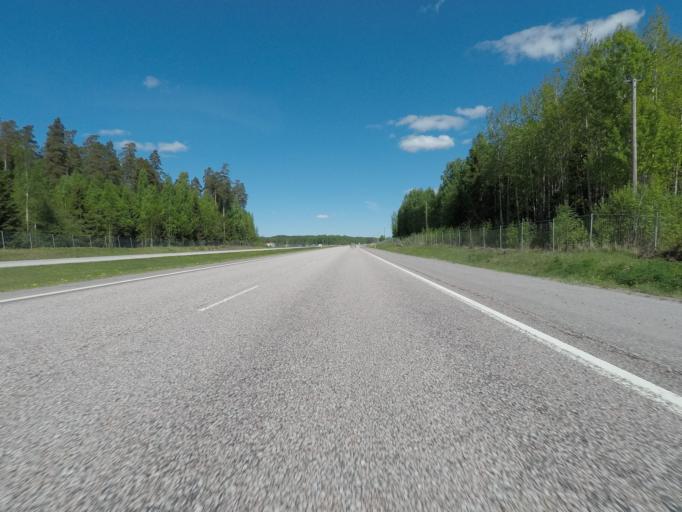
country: FI
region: Uusimaa
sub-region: Helsinki
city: Nurmijaervi
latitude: 60.4748
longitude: 24.8497
